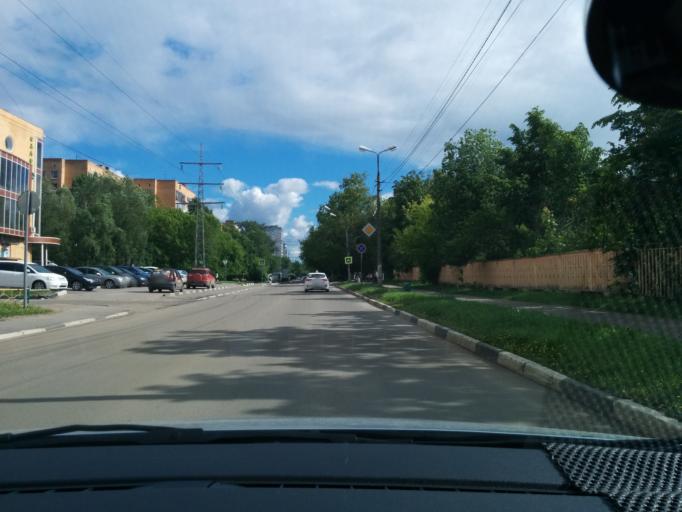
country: RU
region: Moskovskaya
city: Lobnya
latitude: 56.0160
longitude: 37.4791
